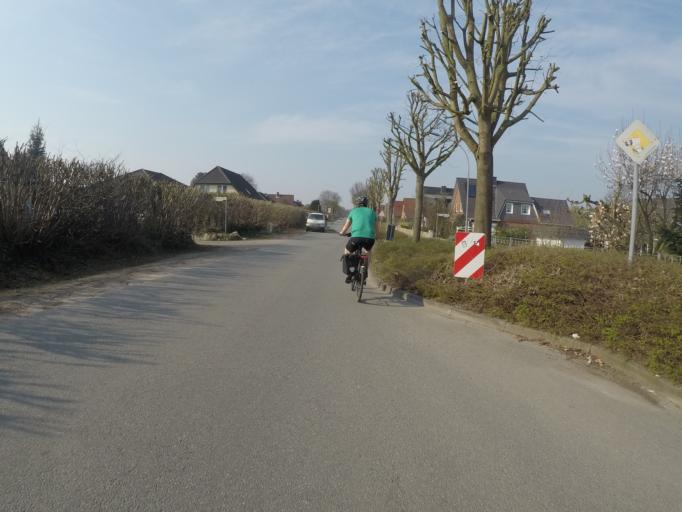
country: DE
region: Schleswig-Holstein
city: Kukels
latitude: 53.9001
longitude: 10.2331
